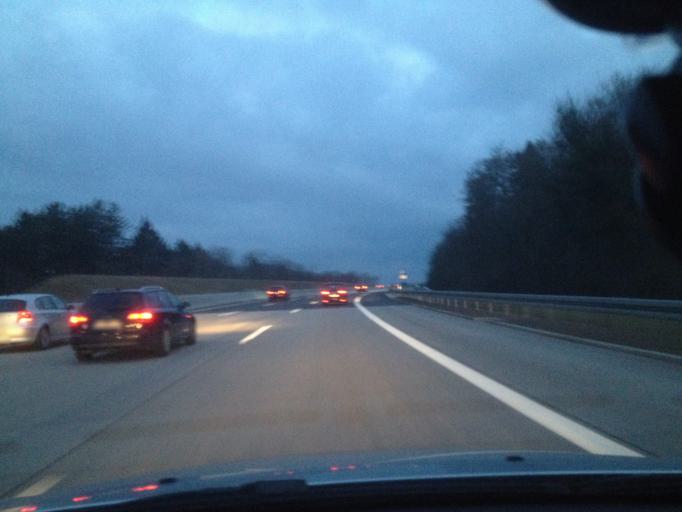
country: DE
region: Baden-Wuerttemberg
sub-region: Karlsruhe Region
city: Konigsbach-Stein
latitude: 48.9185
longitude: 8.6127
